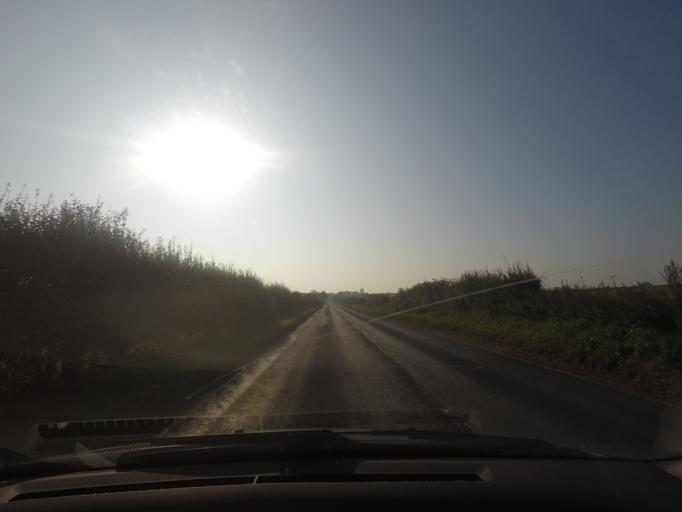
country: GB
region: England
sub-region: City and Borough of Leeds
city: Walton
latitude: 54.0115
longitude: -1.3085
